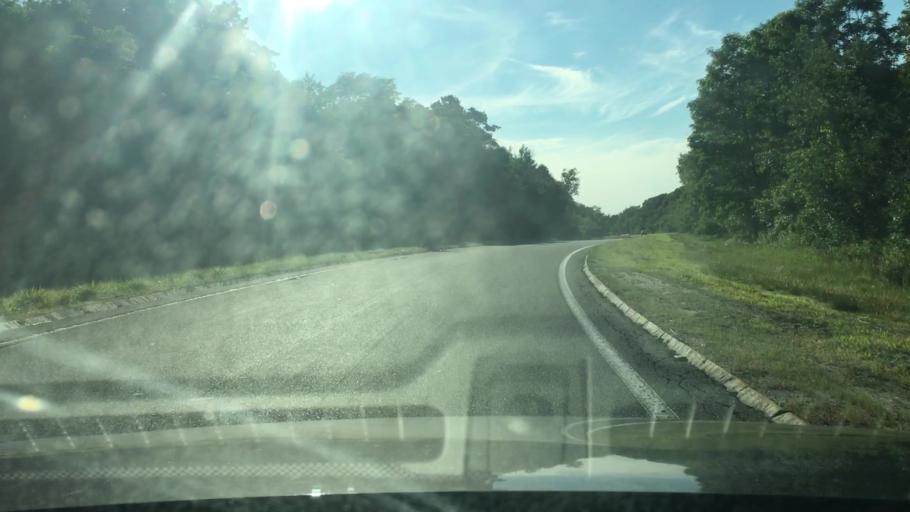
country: US
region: Massachusetts
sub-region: Essex County
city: South Peabody
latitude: 42.5263
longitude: -70.9697
